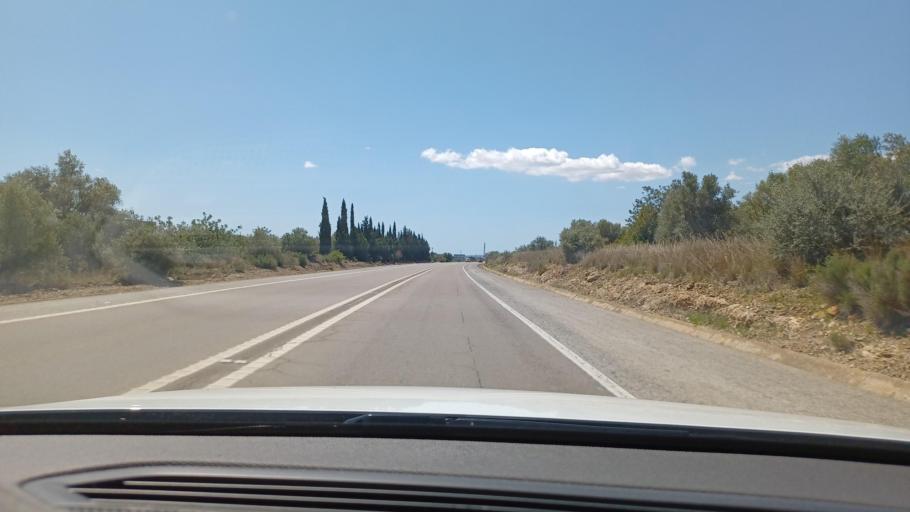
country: ES
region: Catalonia
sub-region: Provincia de Tarragona
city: Camarles
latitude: 40.7961
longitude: 0.6771
